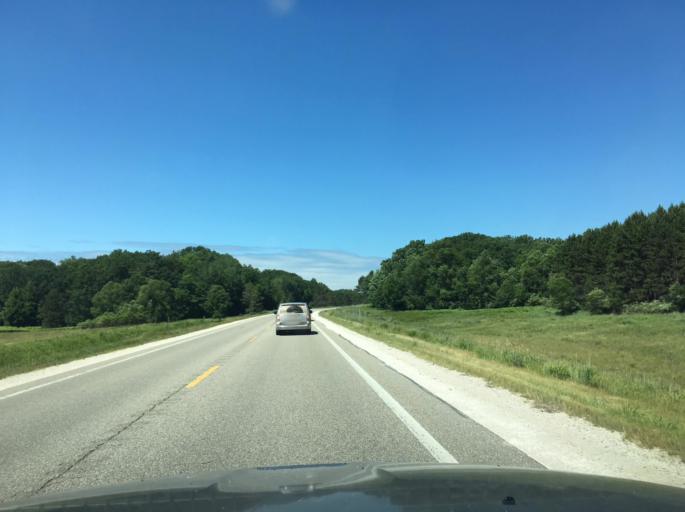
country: US
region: Michigan
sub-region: Osceola County
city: Reed City
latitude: 43.8923
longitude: -85.6682
